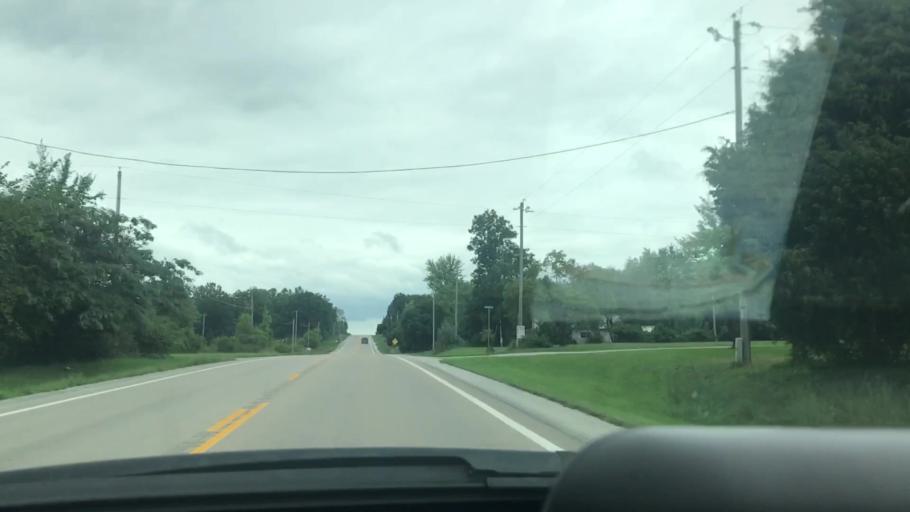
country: US
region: Missouri
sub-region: Dallas County
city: Buffalo
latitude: 37.6991
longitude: -93.1058
